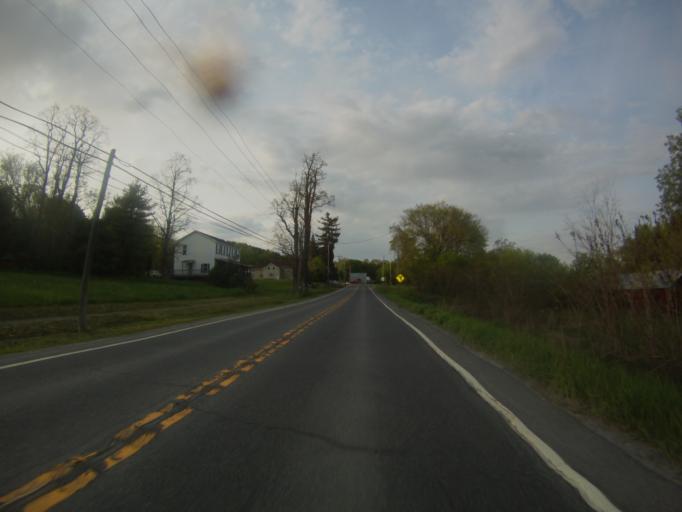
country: US
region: New York
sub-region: Essex County
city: Ticonderoga
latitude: 43.8838
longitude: -73.4487
